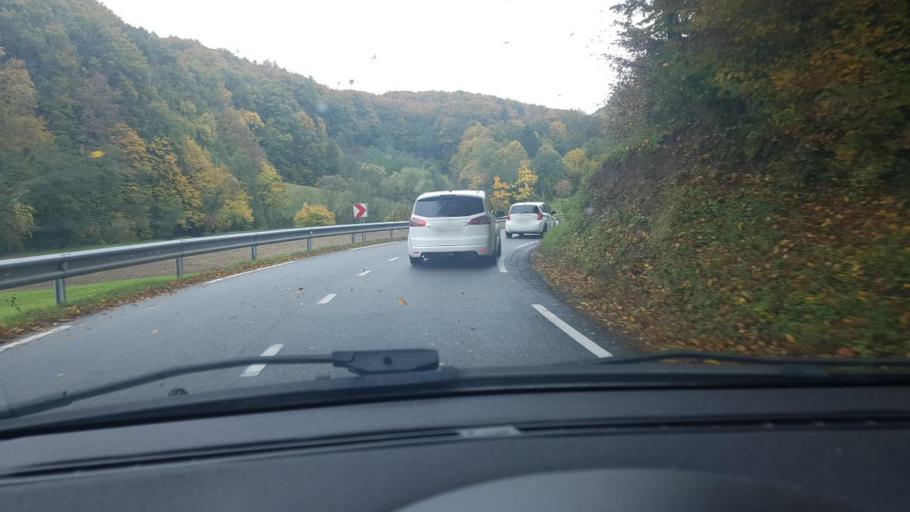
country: SI
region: Majsperk
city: Majsperk
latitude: 46.3275
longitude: 15.7226
